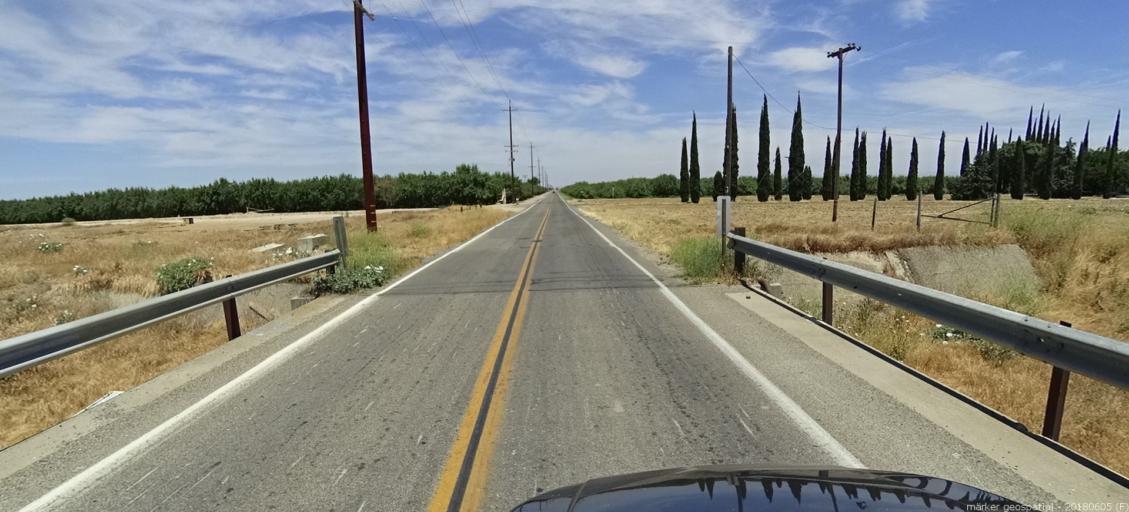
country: US
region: California
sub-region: Madera County
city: Chowchilla
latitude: 37.1209
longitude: -120.3109
